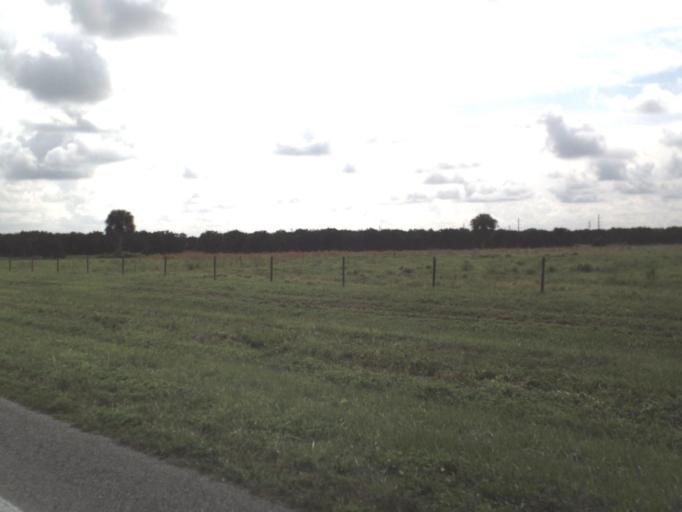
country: US
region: Florida
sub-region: Lee County
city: Alva
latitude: 26.7090
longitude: -81.5922
